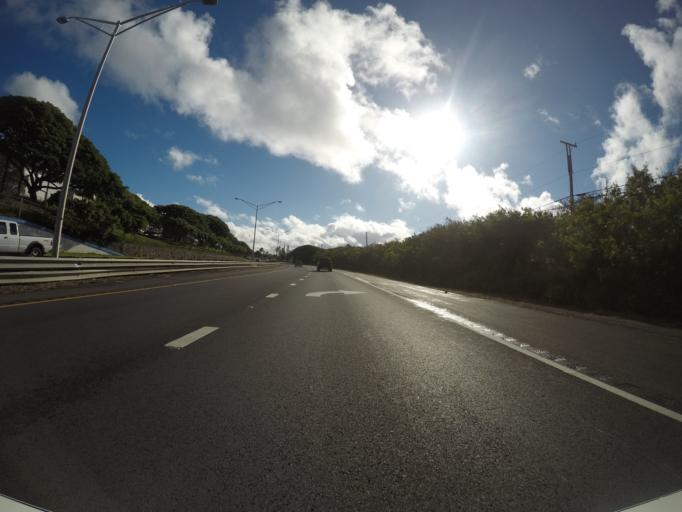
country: US
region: Hawaii
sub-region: Honolulu County
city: Kailua
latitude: 21.4072
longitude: -157.7573
